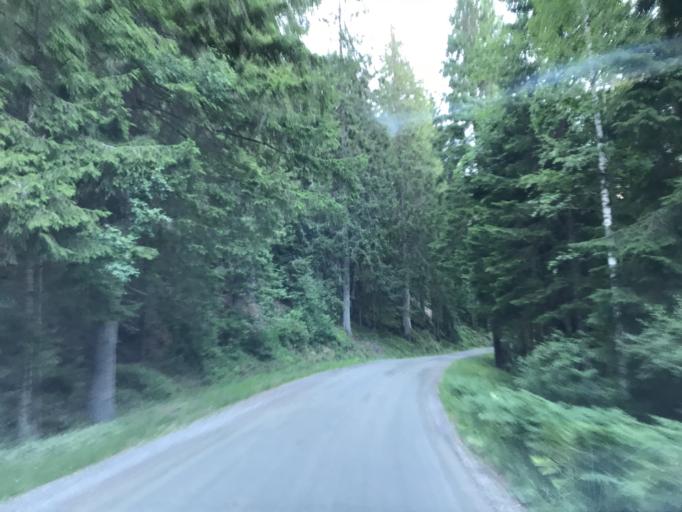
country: SE
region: Vaestra Goetaland
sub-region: Bollebygds Kommun
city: Bollebygd
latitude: 57.7825
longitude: 12.6024
